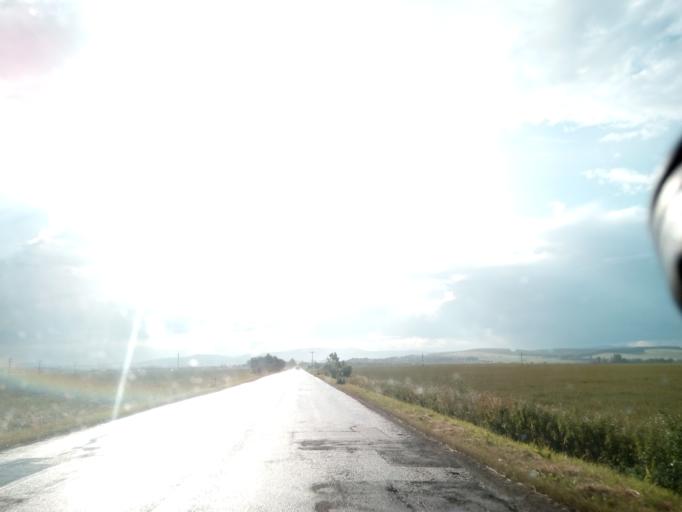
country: SK
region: Kosicky
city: Kosice
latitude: 48.6608
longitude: 21.3450
